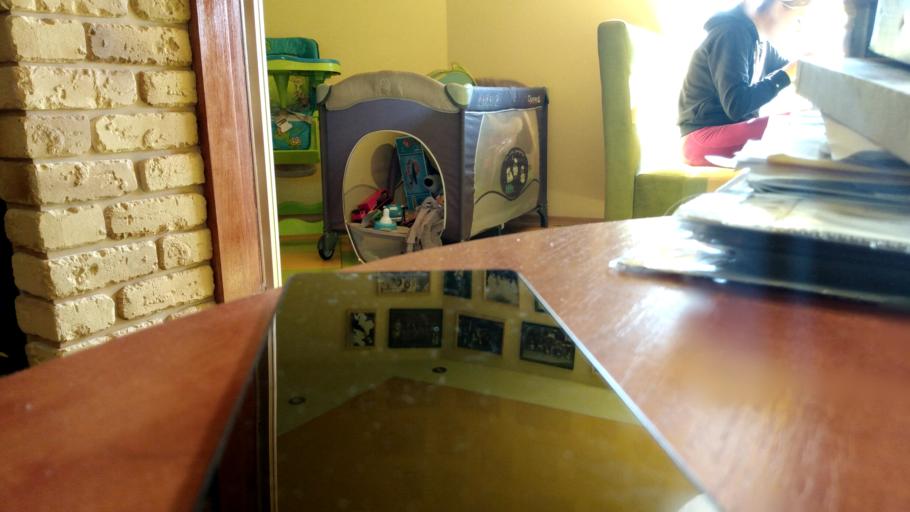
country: RU
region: Penza
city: Serdobsk
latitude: 52.4189
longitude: 44.3143
